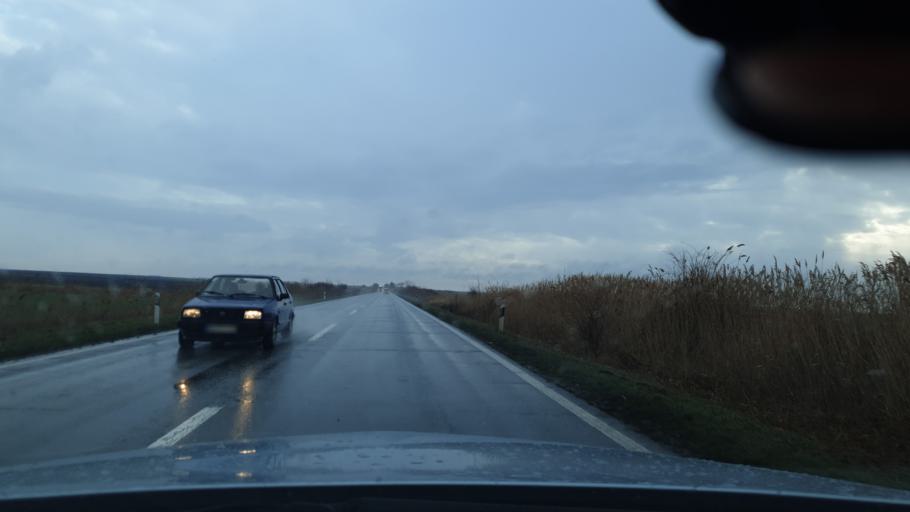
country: RS
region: Autonomna Pokrajina Vojvodina
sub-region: Juznobanatski Okrug
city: Pancevo
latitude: 44.8373
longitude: 20.8094
